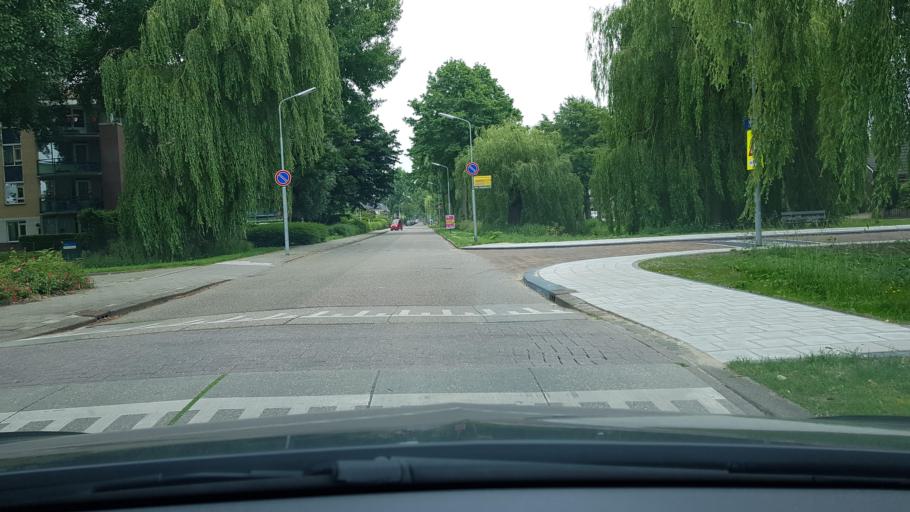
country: NL
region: North Holland
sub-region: Gemeente Aalsmeer
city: Aalsmeer
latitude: 52.3435
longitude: 4.7752
